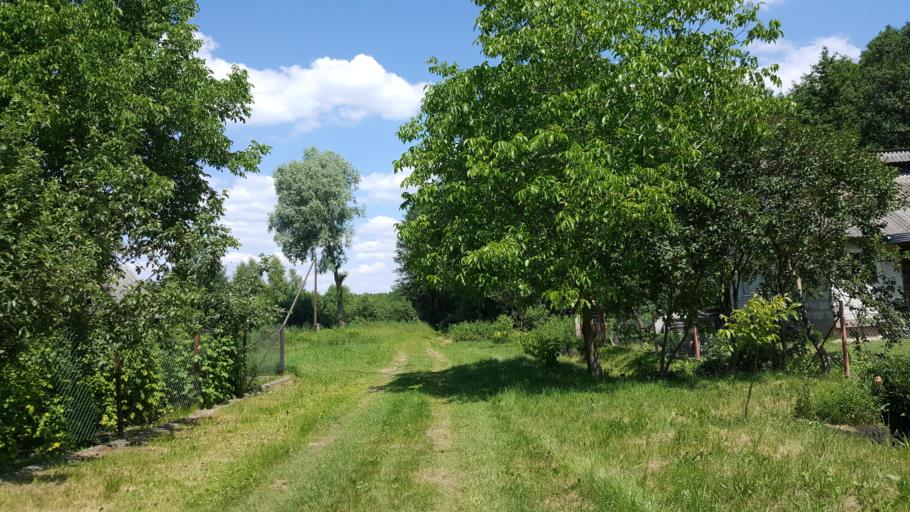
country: BY
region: Brest
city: Kamyanyets
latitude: 52.4133
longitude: 23.8283
